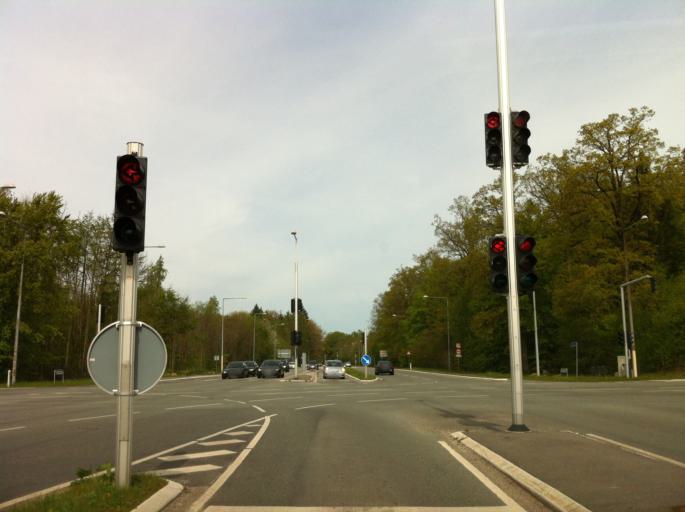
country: DK
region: Capital Region
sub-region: Hillerod Kommune
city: Hillerod
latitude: 55.9214
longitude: 12.3311
